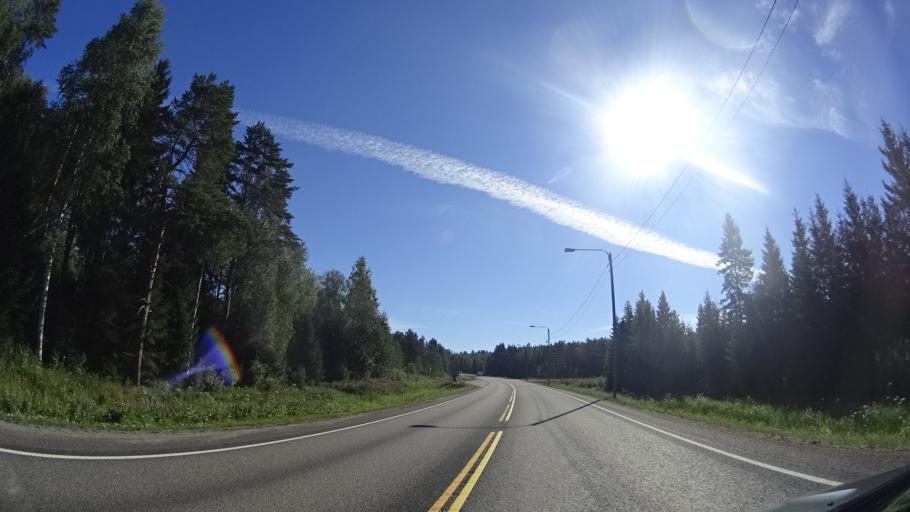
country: FI
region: Central Finland
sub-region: Jyvaeskylae
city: Petaejaevesi
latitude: 62.2701
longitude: 25.3372
